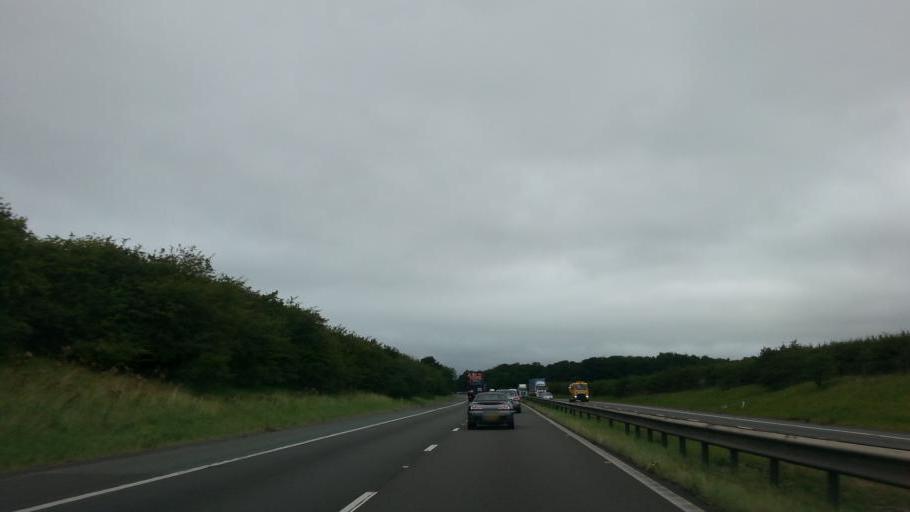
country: GB
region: England
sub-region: Doncaster
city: Tickhill
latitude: 53.4404
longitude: -1.1021
